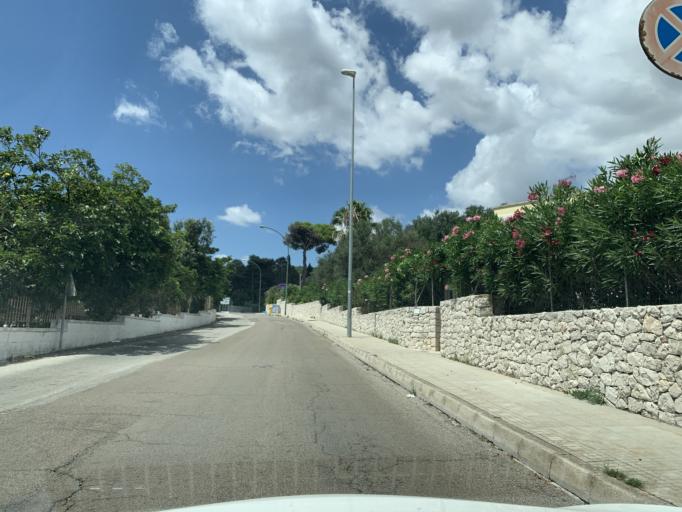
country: IT
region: Apulia
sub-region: Provincia di Lecce
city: Santa Cesarea Terme
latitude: 40.0327
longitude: 18.4482
